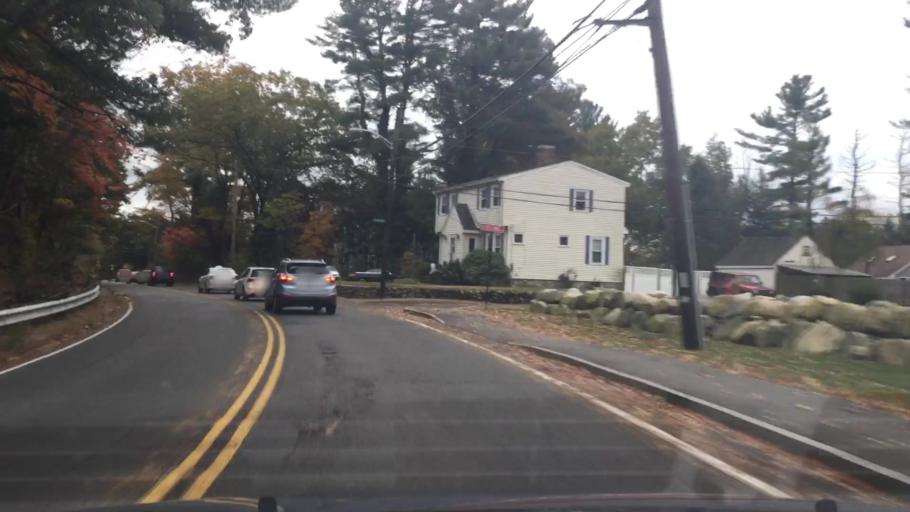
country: US
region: Massachusetts
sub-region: Essex County
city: Saugus
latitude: 42.5025
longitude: -71.0228
